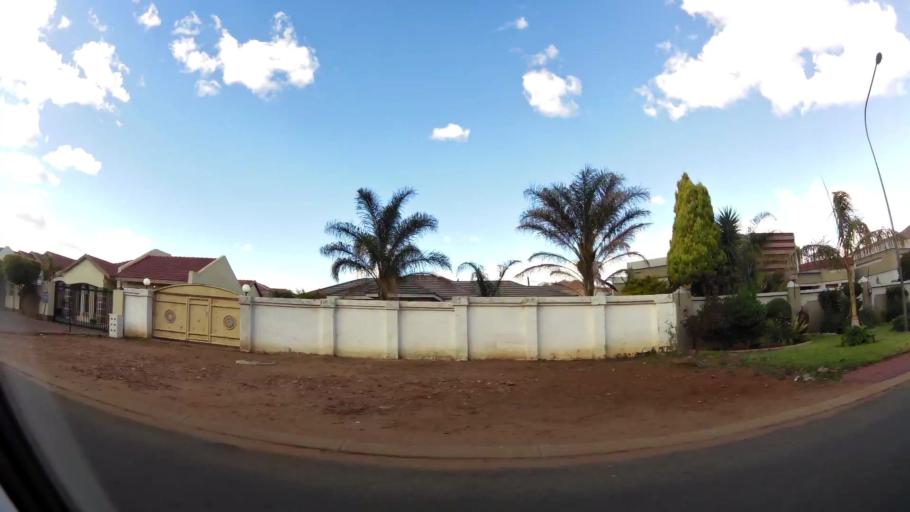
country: ZA
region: Limpopo
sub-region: Capricorn District Municipality
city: Polokwane
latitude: -23.9161
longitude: 29.4945
